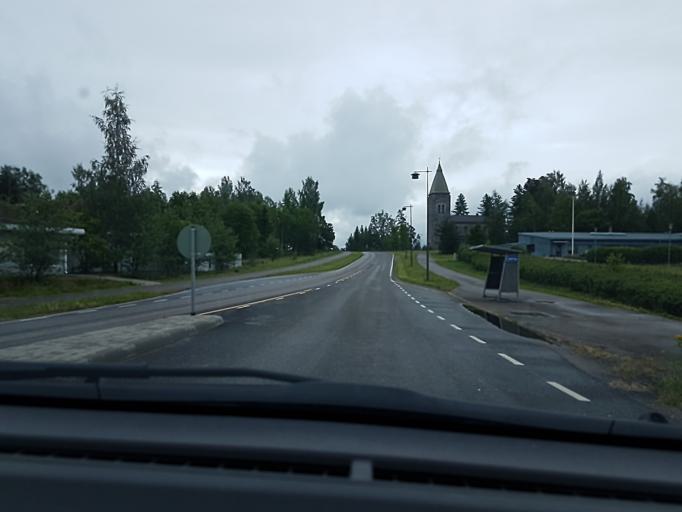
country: FI
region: Uusimaa
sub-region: Helsinki
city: Pornainen
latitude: 60.4757
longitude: 25.3751
